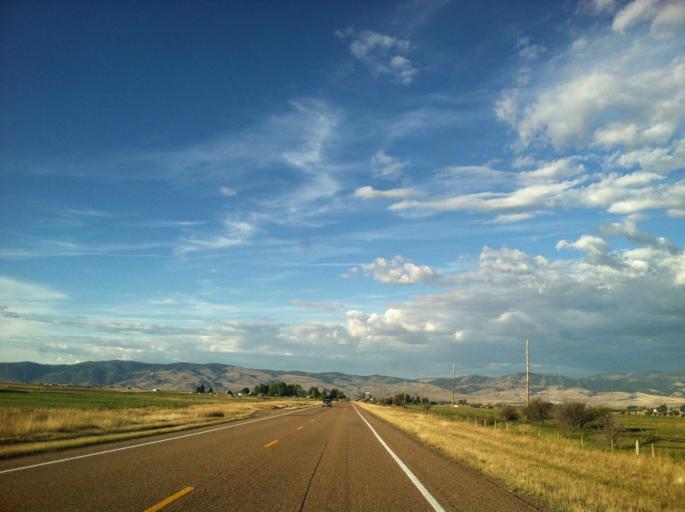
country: US
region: Montana
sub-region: Granite County
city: Philipsburg
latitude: 46.5758
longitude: -113.2031
